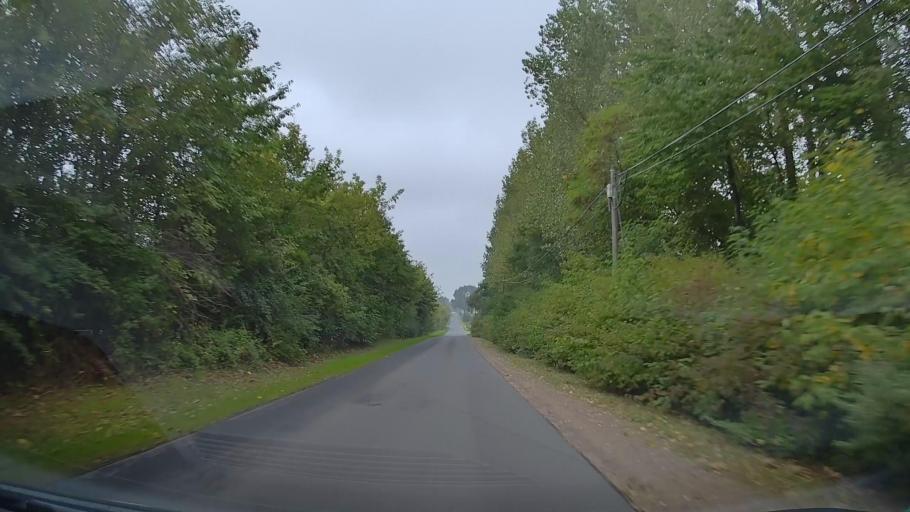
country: DE
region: Mecklenburg-Vorpommern
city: Neubukow
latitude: 54.0490
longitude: 11.6181
